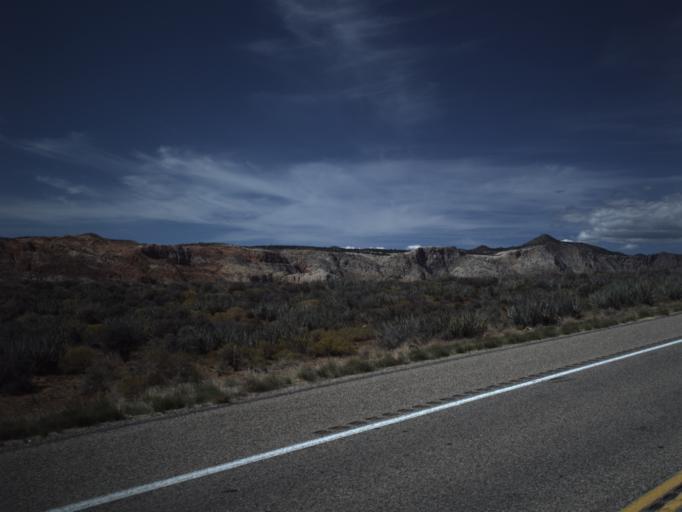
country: US
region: Utah
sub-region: Washington County
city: Ivins
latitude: 37.2149
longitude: -113.6323
